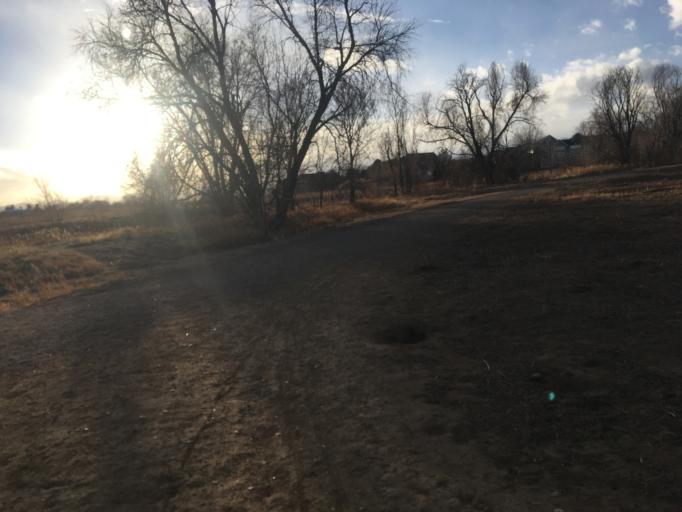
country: US
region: Colorado
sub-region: Boulder County
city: Lafayette
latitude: 40.0052
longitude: -105.0843
